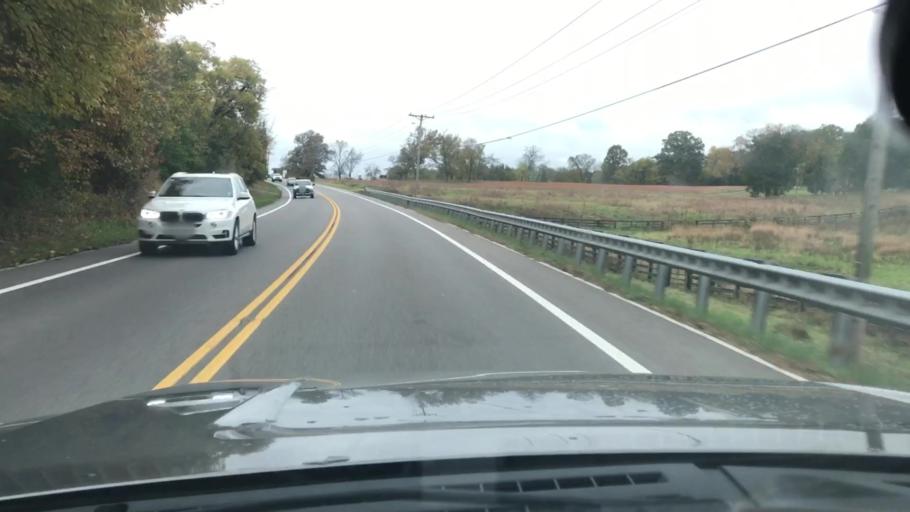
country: US
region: Tennessee
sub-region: Williamson County
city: Franklin
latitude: 35.9903
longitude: -86.8903
